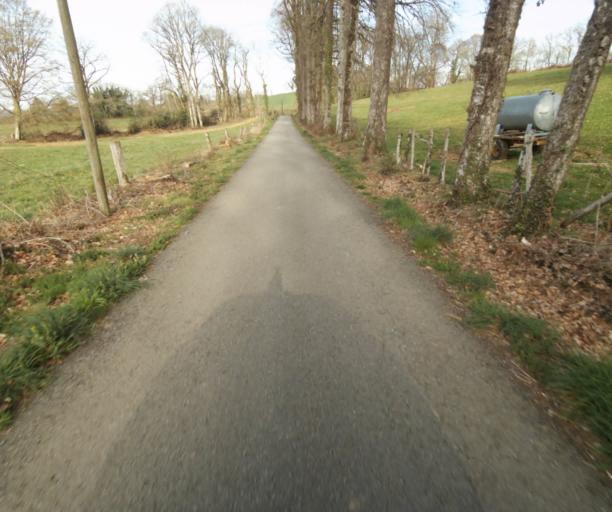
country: FR
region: Limousin
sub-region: Departement de la Correze
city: Chamboulive
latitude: 45.4281
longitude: 1.7494
